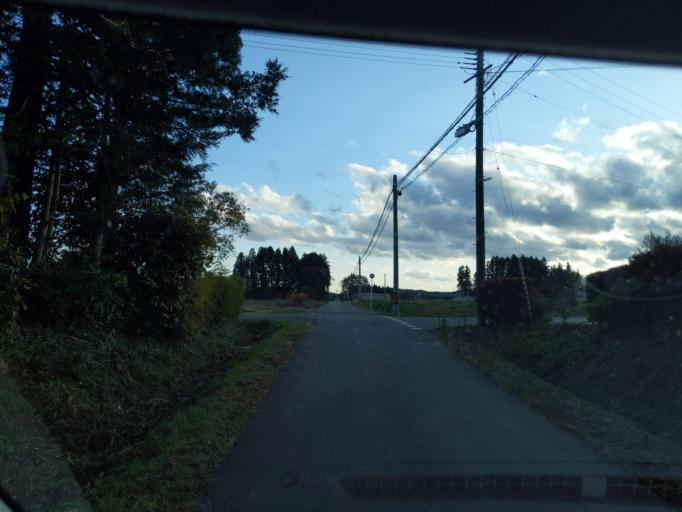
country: JP
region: Iwate
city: Mizusawa
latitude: 39.0925
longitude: 141.0378
